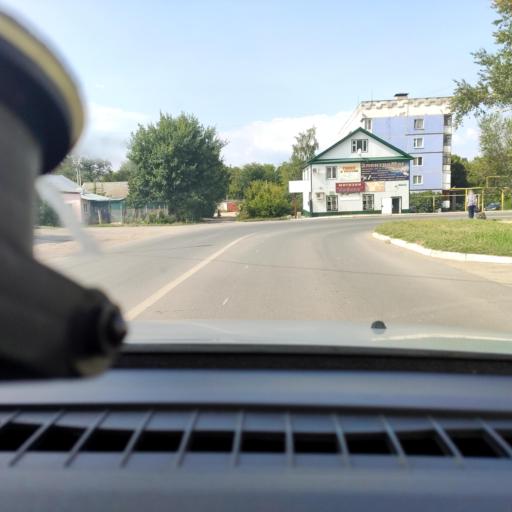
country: RU
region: Samara
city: Chapayevsk
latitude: 52.9574
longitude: 49.6807
